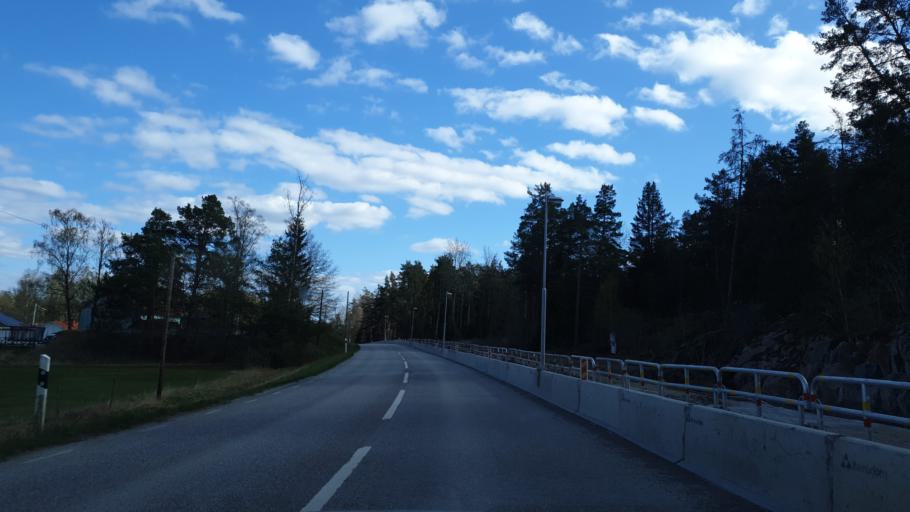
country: SE
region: Stockholm
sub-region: Sigtuna Kommun
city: Rosersberg
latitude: 59.5993
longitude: 17.8822
